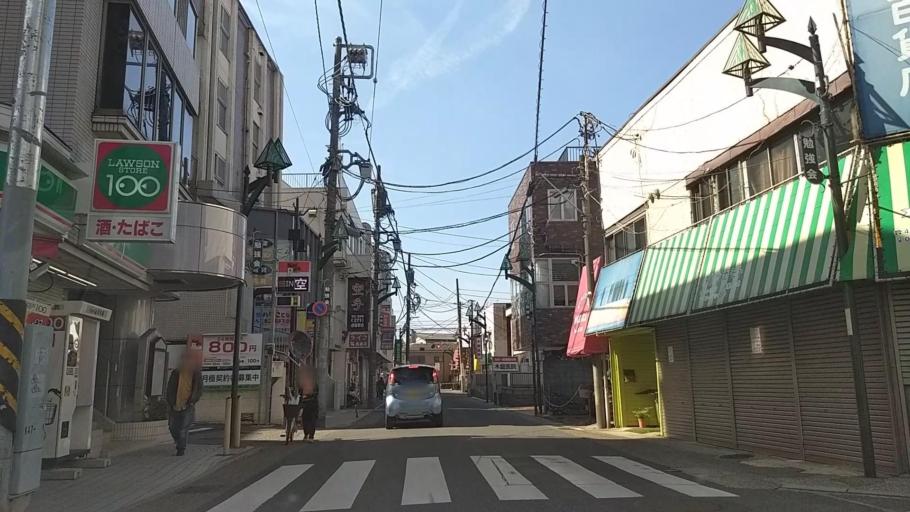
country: JP
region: Kanagawa
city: Fujisawa
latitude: 35.4135
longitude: 139.4664
